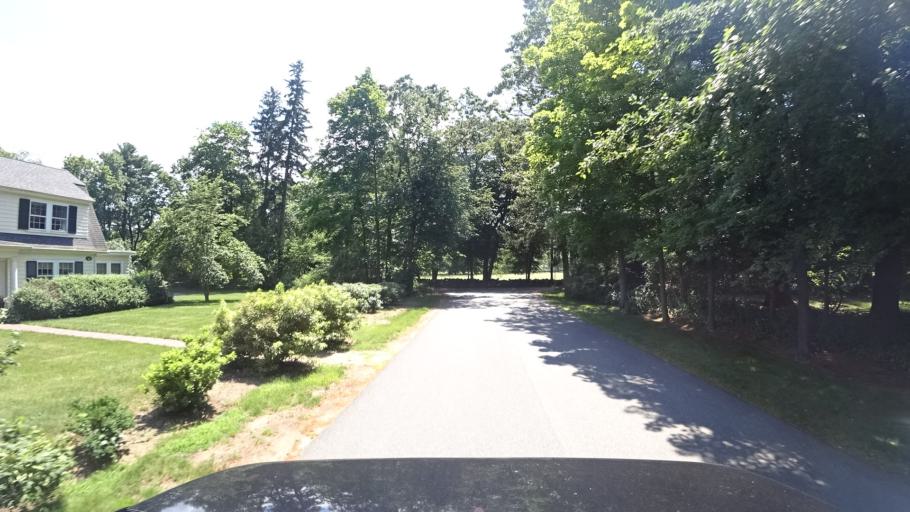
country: US
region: Massachusetts
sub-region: Norfolk County
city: Dedham
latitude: 42.2516
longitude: -71.1900
